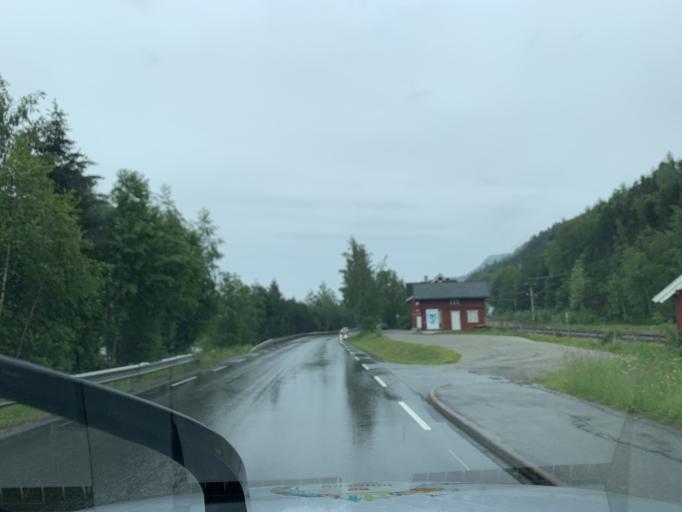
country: NO
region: Oppland
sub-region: Ringebu
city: Ringebu
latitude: 61.4501
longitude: 10.1851
